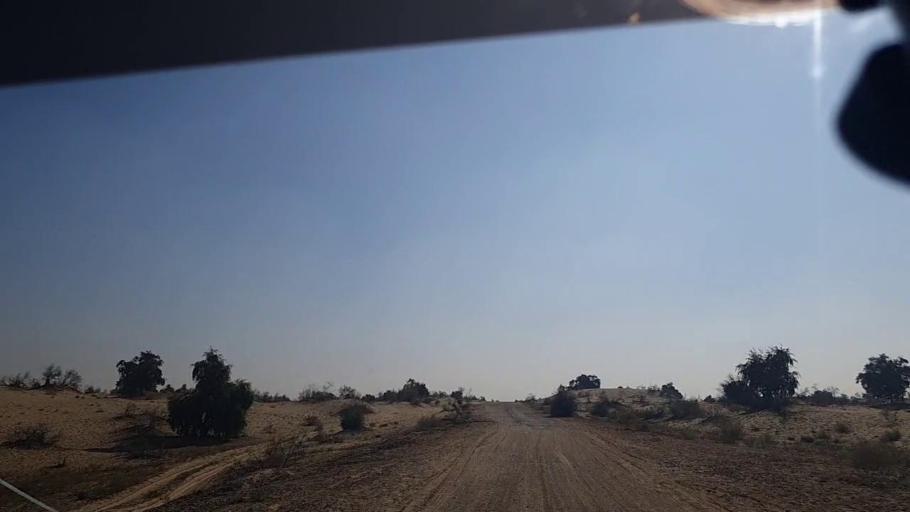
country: PK
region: Sindh
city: Khanpur
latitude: 27.5751
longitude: 69.3055
